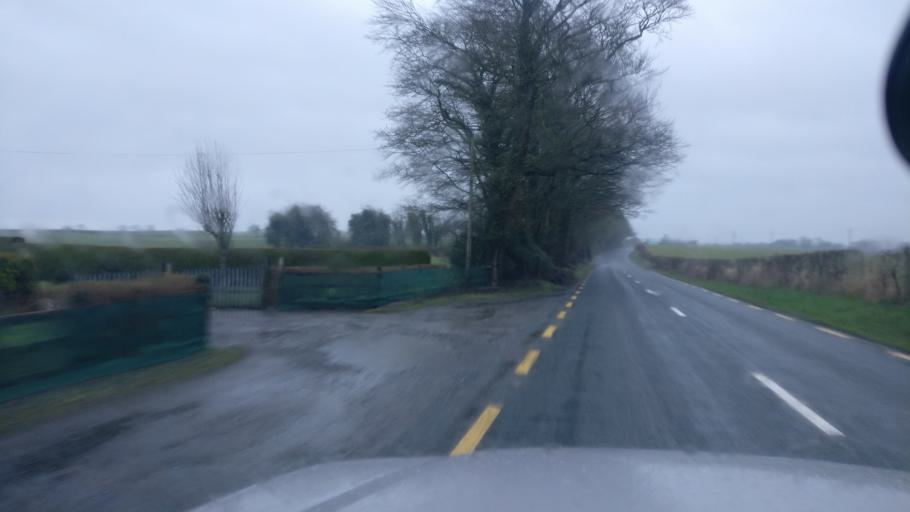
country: IE
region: Connaught
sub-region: County Galway
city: Ballinasloe
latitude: 53.2596
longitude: -8.1850
